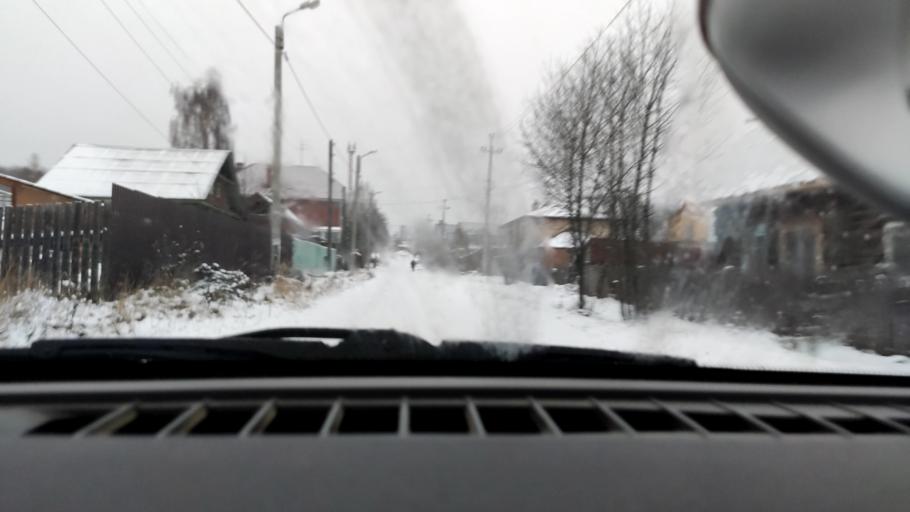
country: RU
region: Perm
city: Kondratovo
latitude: 58.0430
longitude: 56.1137
